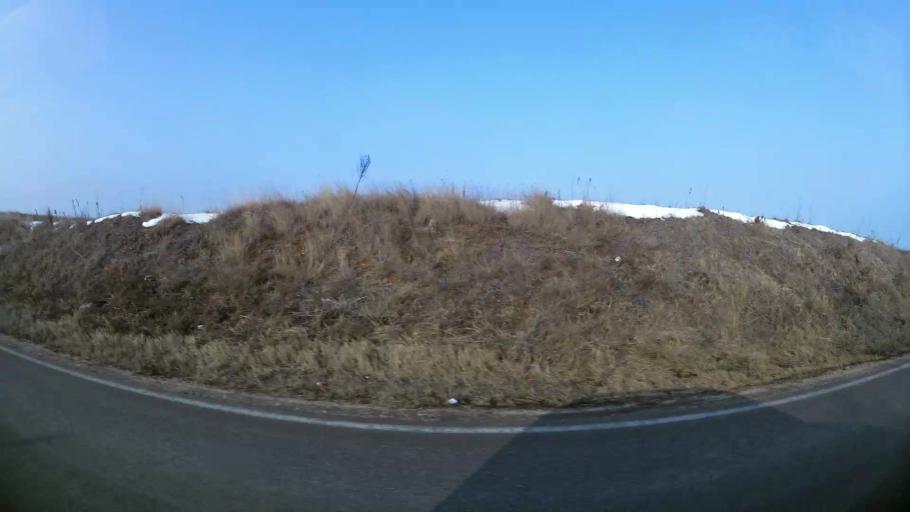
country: MK
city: Miladinovci
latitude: 41.9772
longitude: 21.6270
